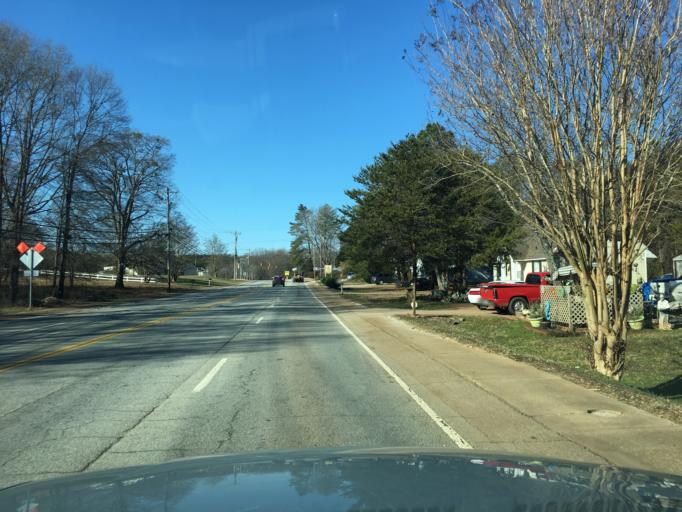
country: US
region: South Carolina
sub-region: Greenville County
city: Berea
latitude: 34.8938
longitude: -82.4422
